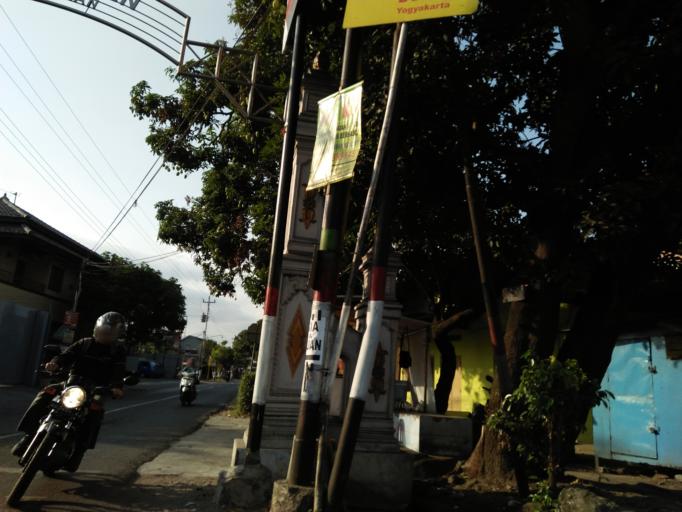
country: ID
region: Daerah Istimewa Yogyakarta
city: Depok
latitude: -7.7819
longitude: 110.4502
